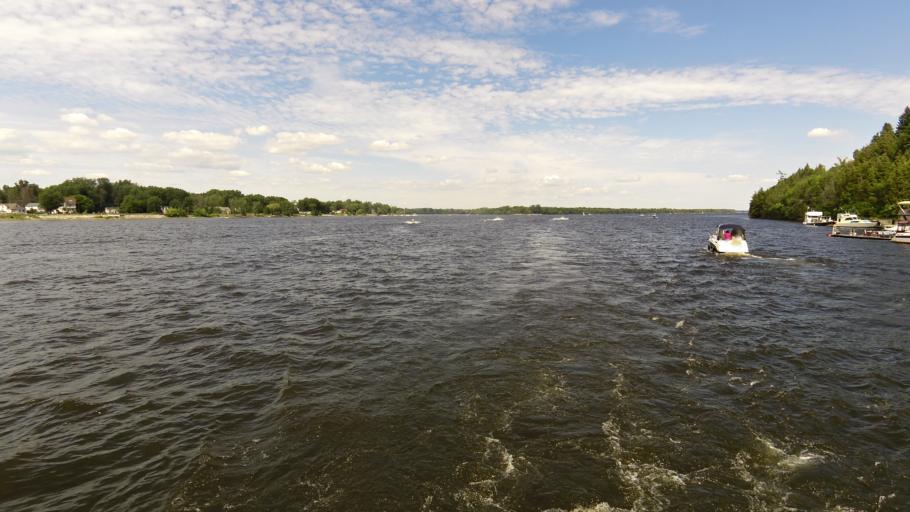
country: CA
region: Quebec
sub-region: Outaouais
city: Gatineau
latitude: 45.4561
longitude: -75.6873
